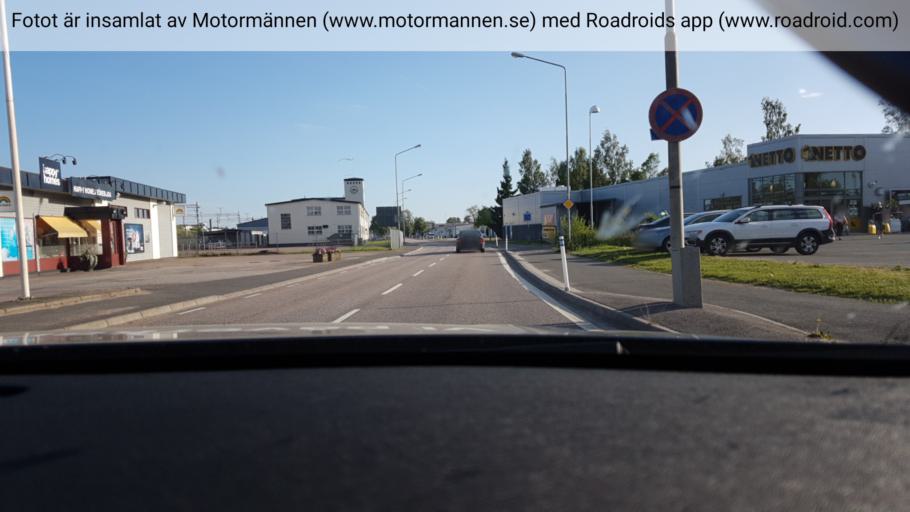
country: SE
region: Vaestra Goetaland
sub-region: Toreboda Kommun
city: Toereboda
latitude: 58.7045
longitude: 14.1251
